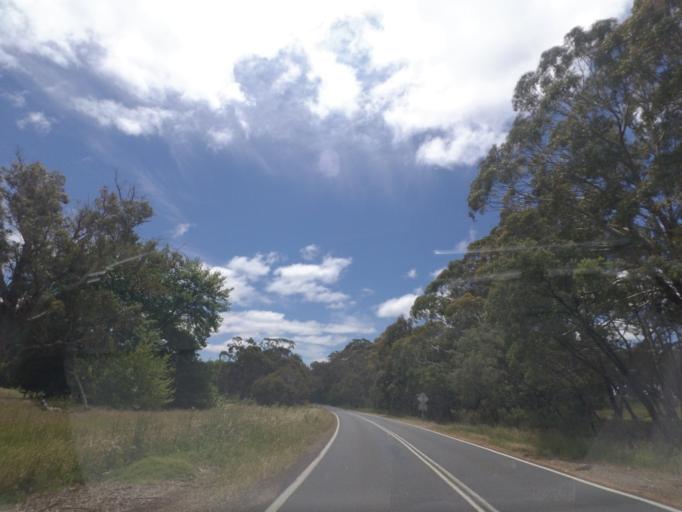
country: AU
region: Victoria
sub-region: Mount Alexander
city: Castlemaine
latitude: -37.3325
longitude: 144.1668
